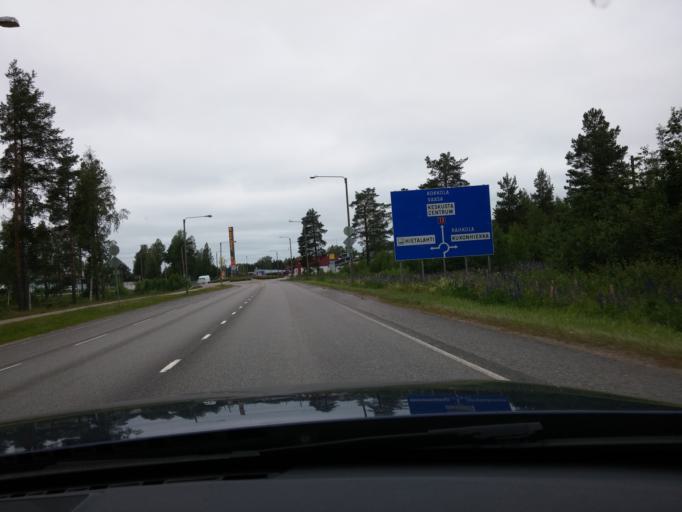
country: FI
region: Central Finland
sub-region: Saarijaervi-Viitasaari
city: Saarijaervi
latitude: 62.6953
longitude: 25.2972
